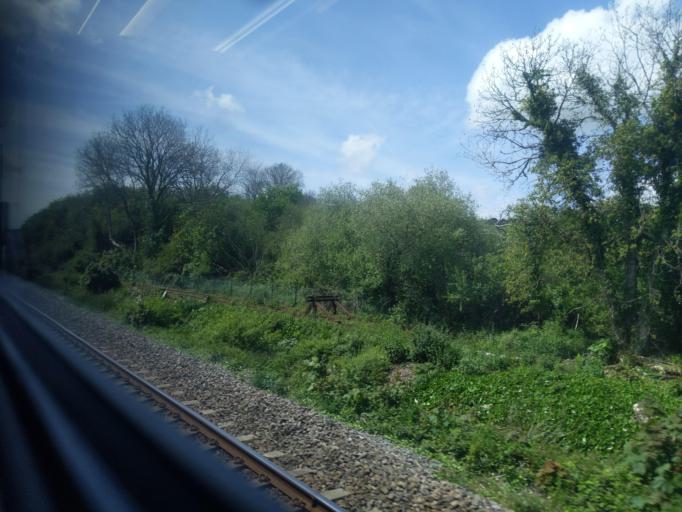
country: GB
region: England
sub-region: Cornwall
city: St Austell
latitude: 50.3398
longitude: -4.8250
